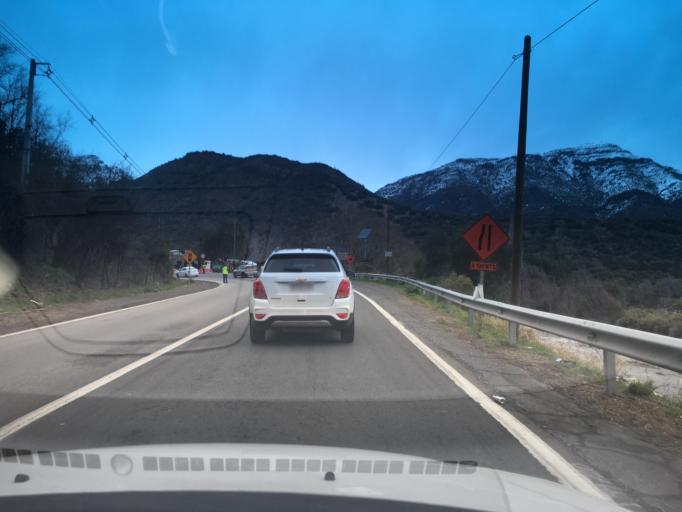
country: CL
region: Santiago Metropolitan
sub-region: Provincia de Cordillera
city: Puente Alto
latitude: -33.6834
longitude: -70.3389
